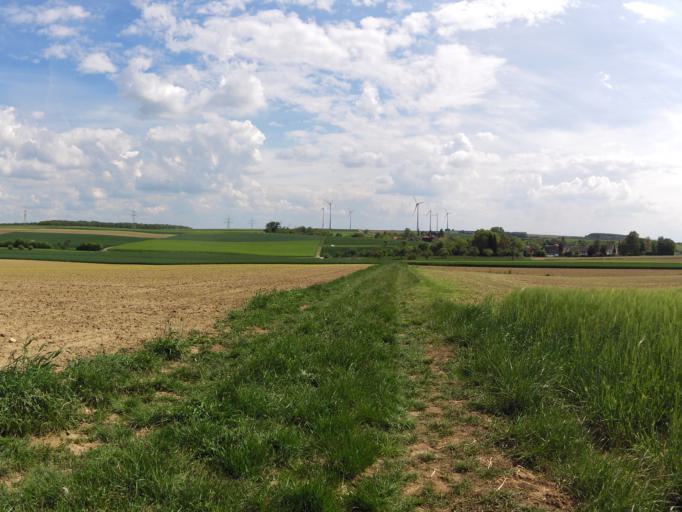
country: DE
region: Bavaria
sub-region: Regierungsbezirk Unterfranken
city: Theilheim
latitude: 49.7393
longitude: 10.0326
